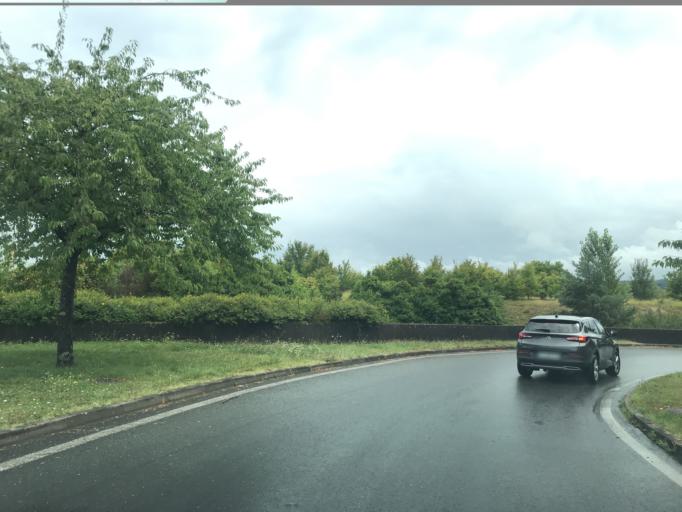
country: FR
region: Aquitaine
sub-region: Departement de la Dordogne
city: Coulounieix-Chamiers
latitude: 45.1558
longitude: 0.7047
